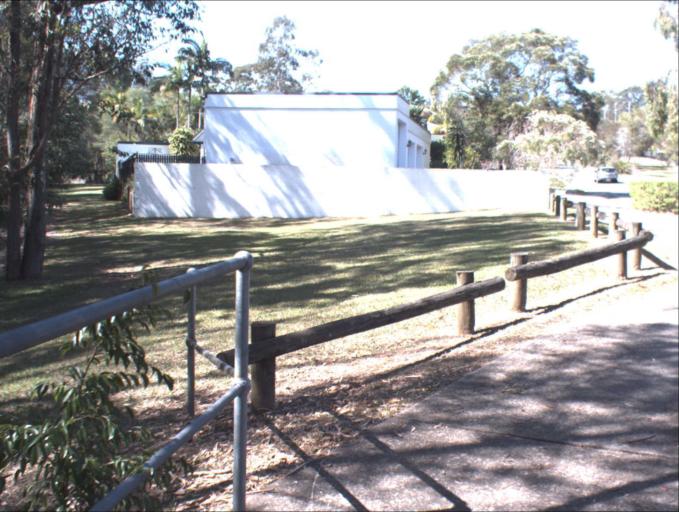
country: AU
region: Queensland
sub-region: Logan
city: Springwood
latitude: -27.6130
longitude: 153.1429
